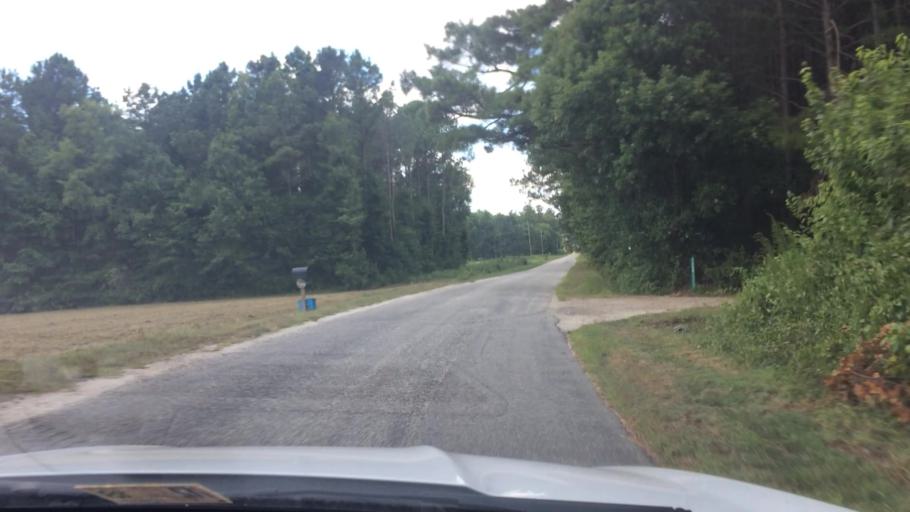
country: US
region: Virginia
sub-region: King William County
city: West Point
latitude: 37.5967
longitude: -76.7928
